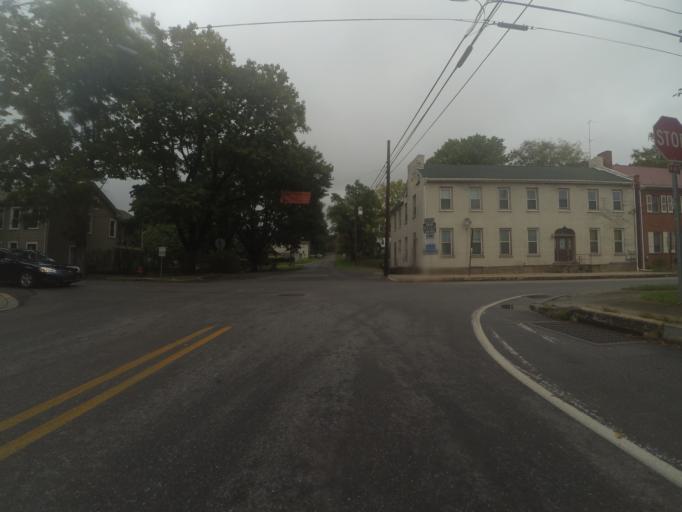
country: US
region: Pennsylvania
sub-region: Huntingdon County
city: McConnellstown
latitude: 40.5567
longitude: -78.0983
